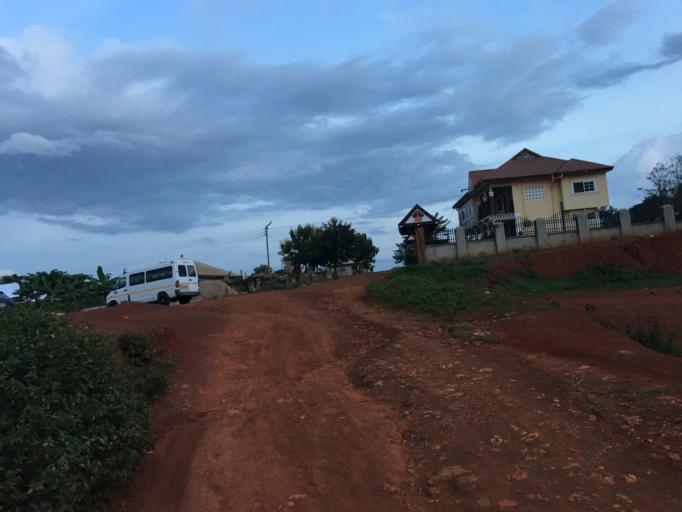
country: GH
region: Western
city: Bibiani
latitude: 6.7869
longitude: -2.5163
